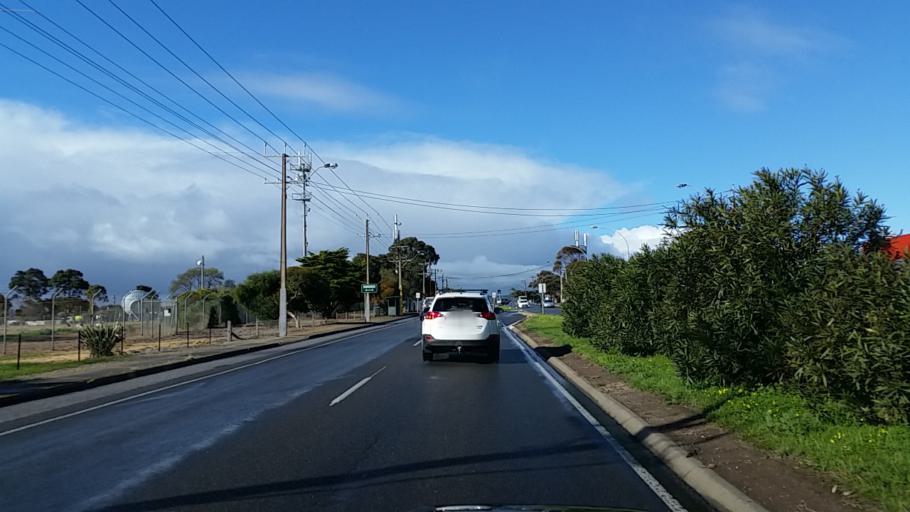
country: AU
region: South Australia
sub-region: Onkaparinga
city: Reynella
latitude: -35.1054
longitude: 138.5196
